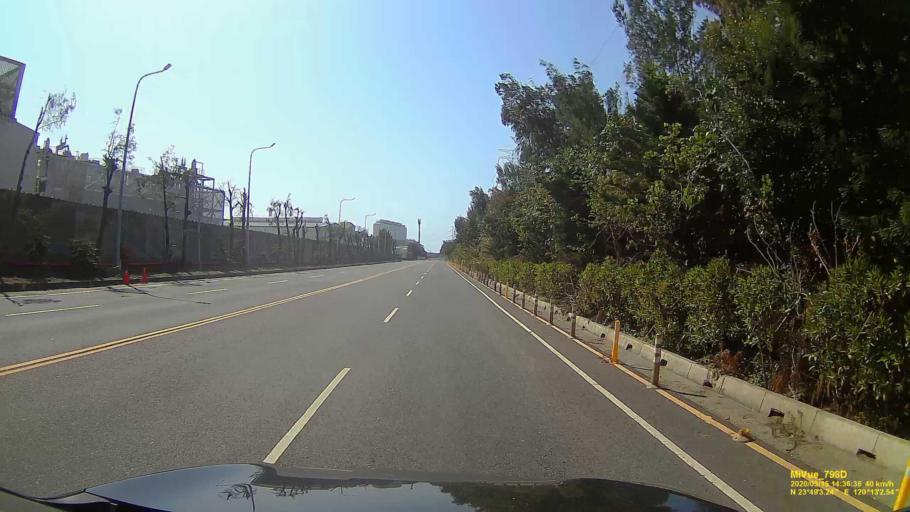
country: TW
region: Taiwan
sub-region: Yunlin
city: Douliu
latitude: 23.8176
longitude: 120.2172
